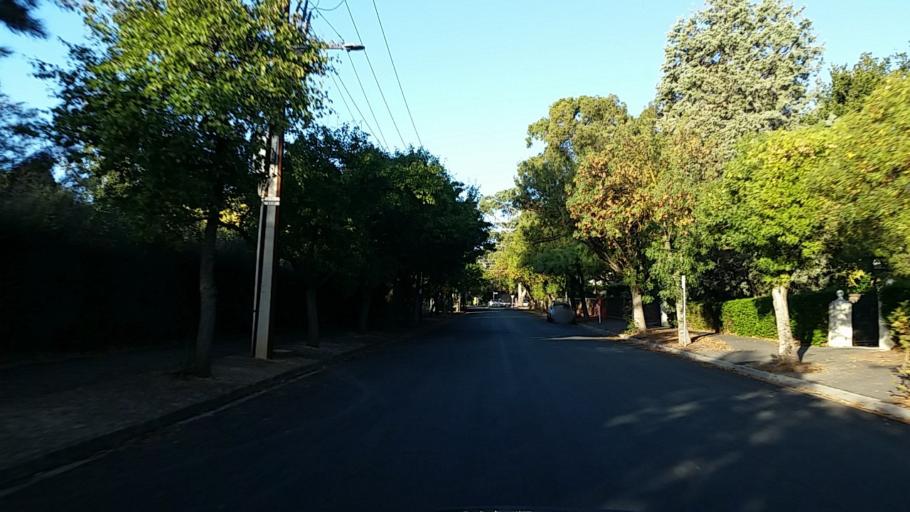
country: AU
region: South Australia
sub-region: Mitcham
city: Mitcham
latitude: -34.9704
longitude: 138.6342
